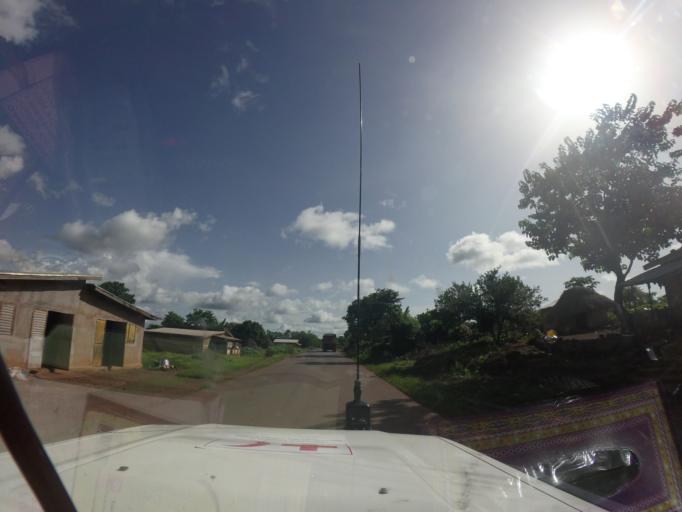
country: GN
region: Mamou
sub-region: Mamou Prefecture
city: Mamou
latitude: 10.2872
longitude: -12.3785
